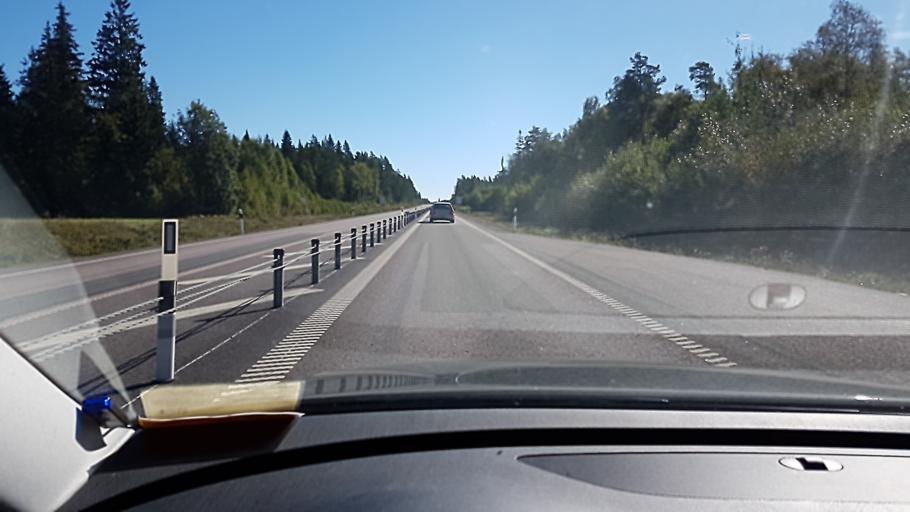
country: SE
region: Kalmar
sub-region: Emmaboda Kommun
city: Emmaboda
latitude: 56.7354
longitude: 15.5267
